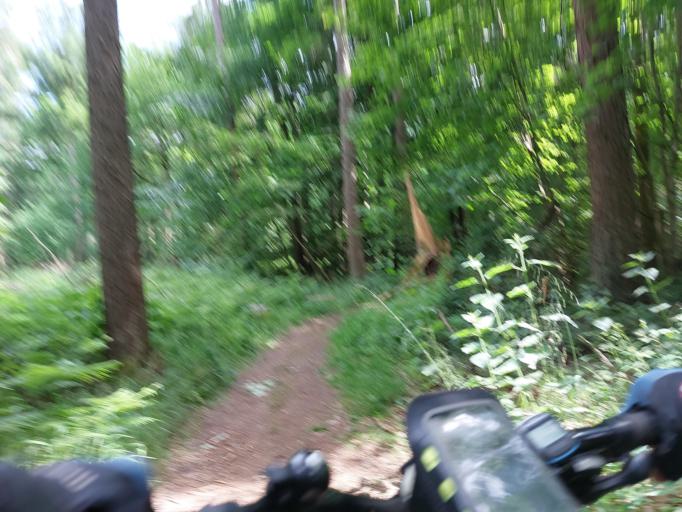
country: BE
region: Wallonia
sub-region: Province du Hainaut
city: Beloeil
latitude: 50.4883
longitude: 3.7523
